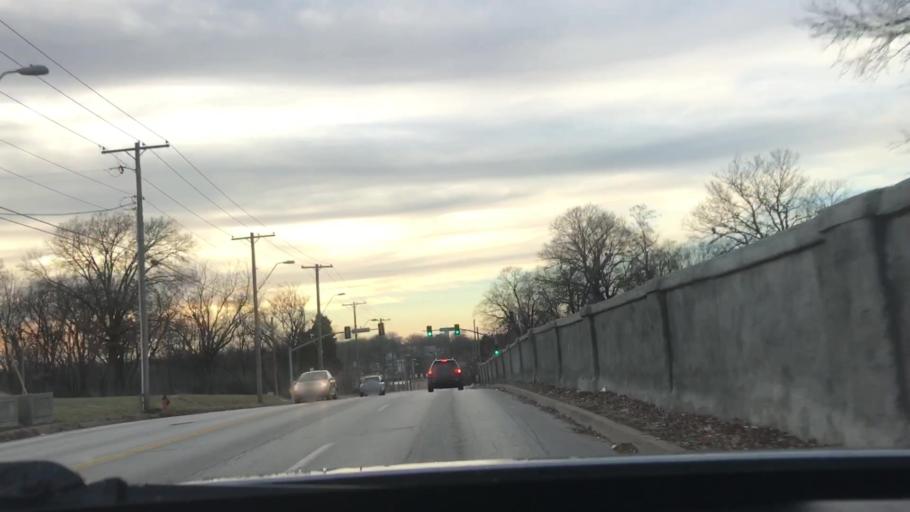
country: US
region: Missouri
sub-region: Jackson County
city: Kansas City
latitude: 39.0839
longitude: -94.5374
